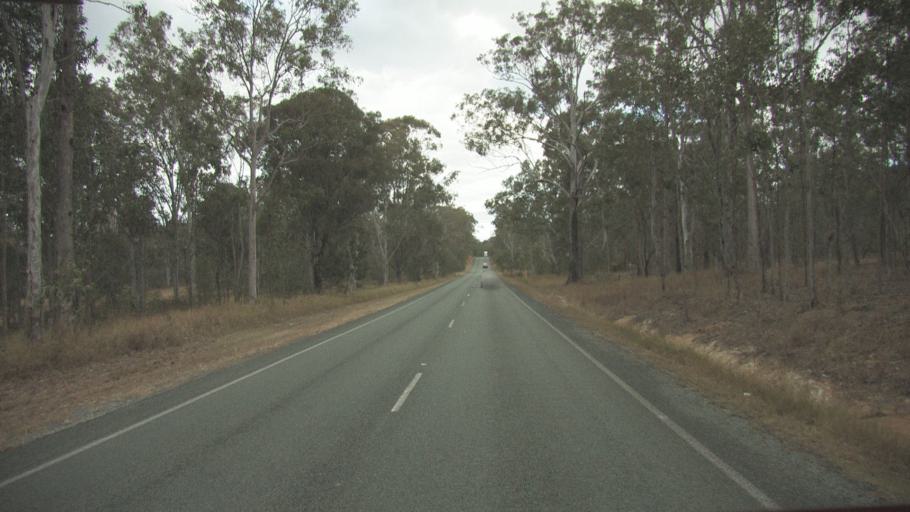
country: AU
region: Queensland
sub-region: Logan
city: Cedar Vale
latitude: -27.9036
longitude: 153.0906
